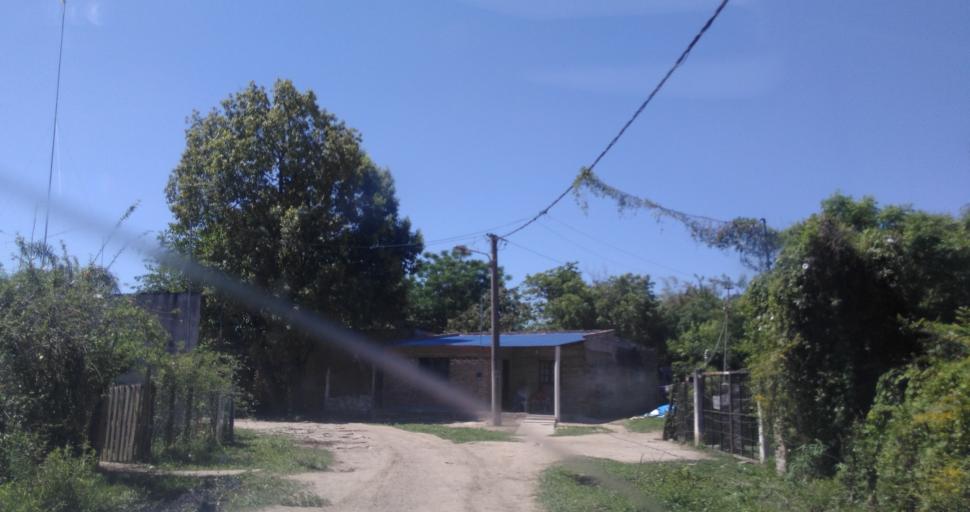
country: AR
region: Chaco
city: Resistencia
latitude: -27.4232
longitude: -58.9805
